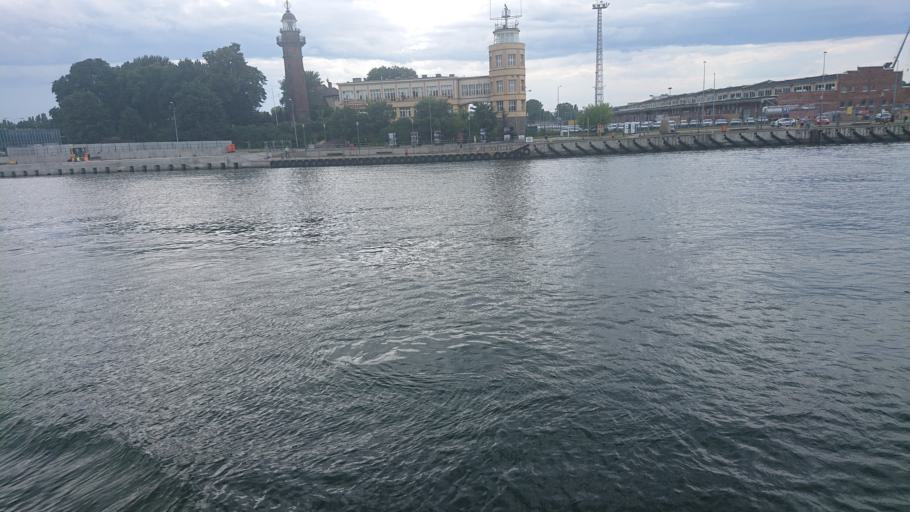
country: PL
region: Pomeranian Voivodeship
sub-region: Gdansk
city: Gdansk
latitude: 54.4074
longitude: 18.6628
